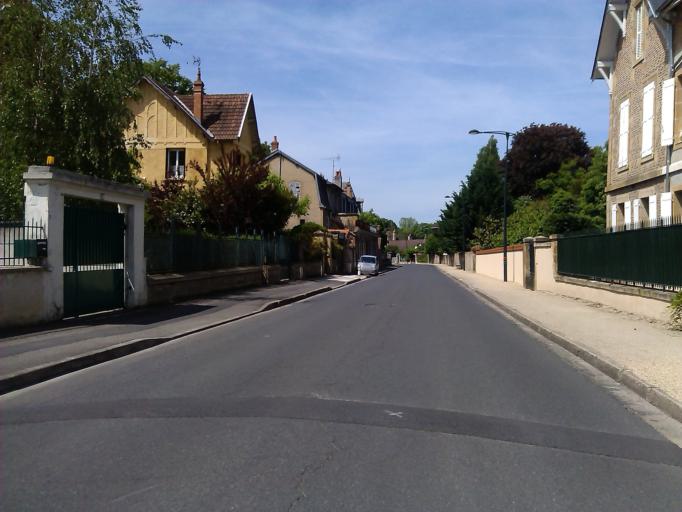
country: FR
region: Auvergne
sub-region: Departement de l'Allier
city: Yzeure
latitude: 46.5667
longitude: 3.3455
